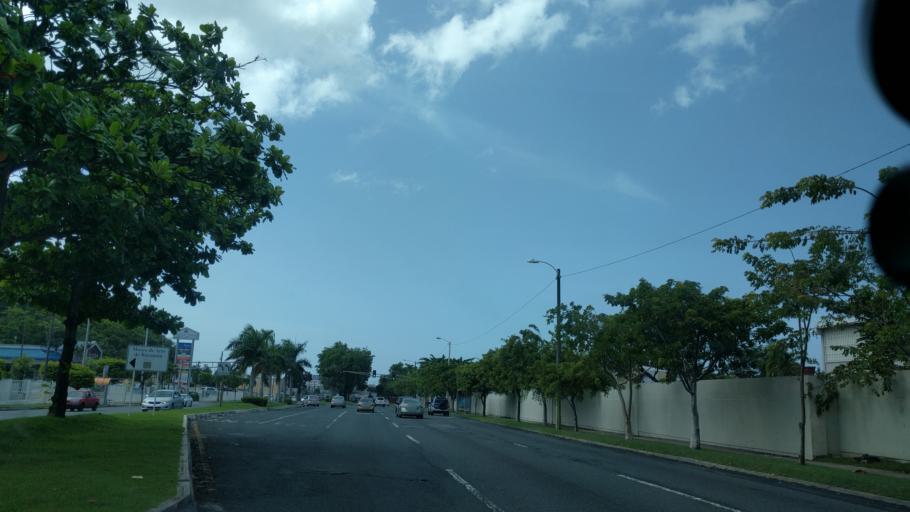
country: PR
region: Bayamon
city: Bayamon
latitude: 18.4120
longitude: -66.1600
